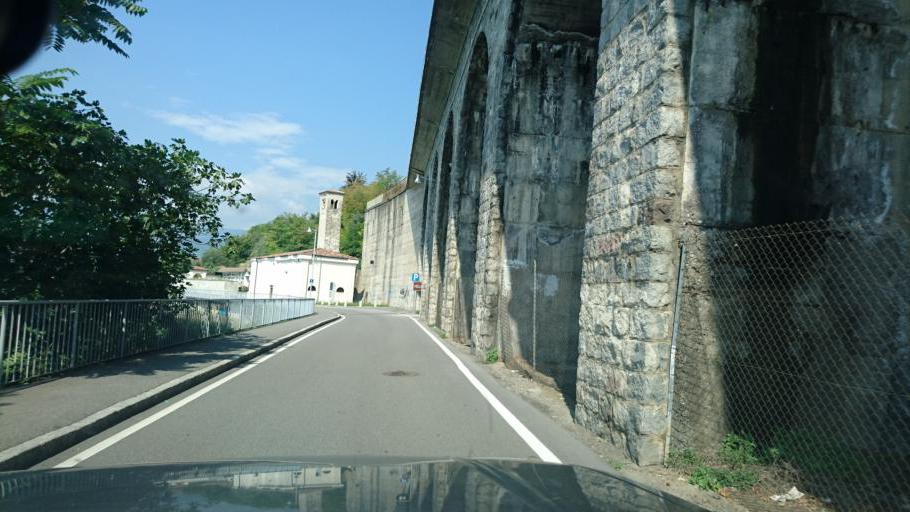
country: IT
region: Lombardy
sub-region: Provincia di Brescia
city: Marone
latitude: 45.7515
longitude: 10.0849
